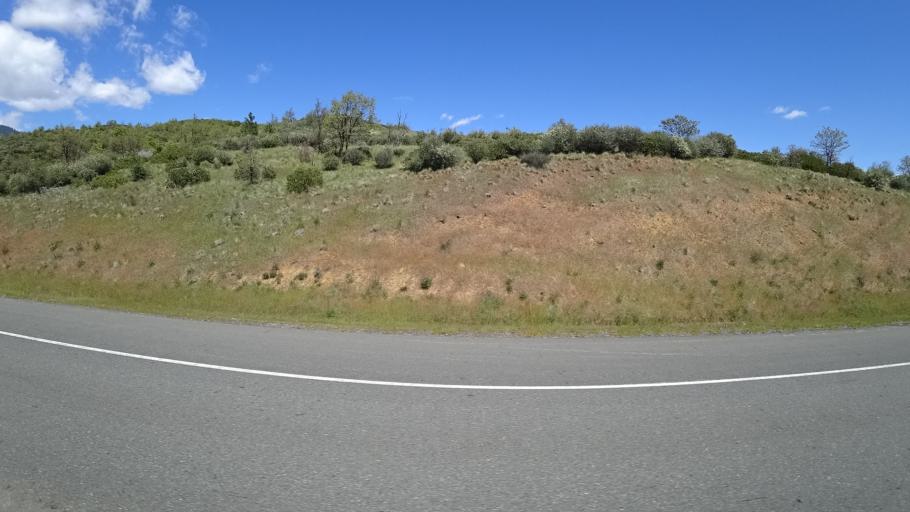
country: US
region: California
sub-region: Trinity County
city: Weaverville
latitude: 40.7383
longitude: -122.9663
